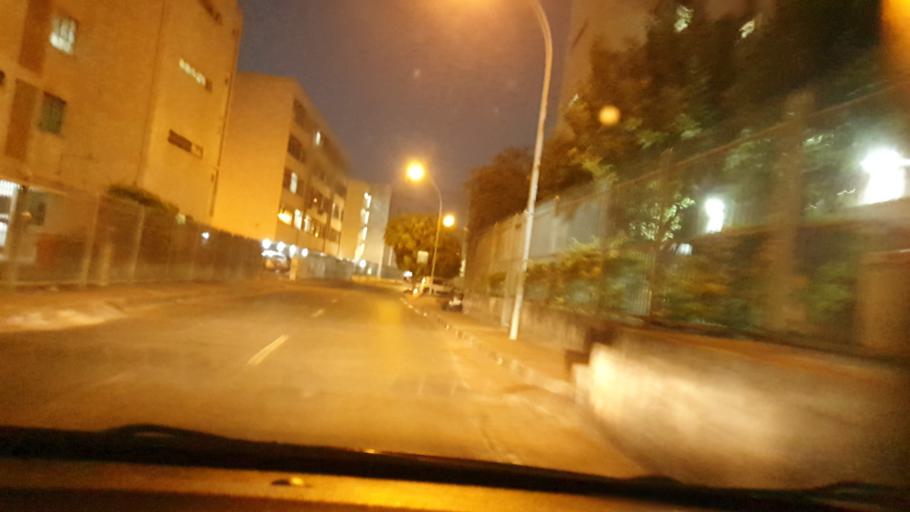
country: BR
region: Federal District
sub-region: Brasilia
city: Brasilia
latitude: -15.7976
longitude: -47.9382
